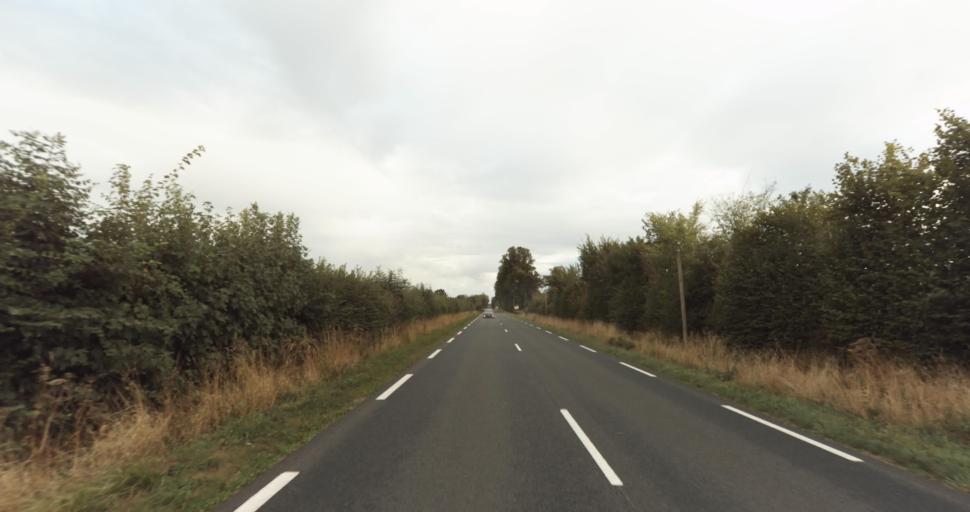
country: FR
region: Lower Normandy
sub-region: Departement de l'Orne
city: Vimoutiers
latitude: 48.8891
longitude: 0.2557
